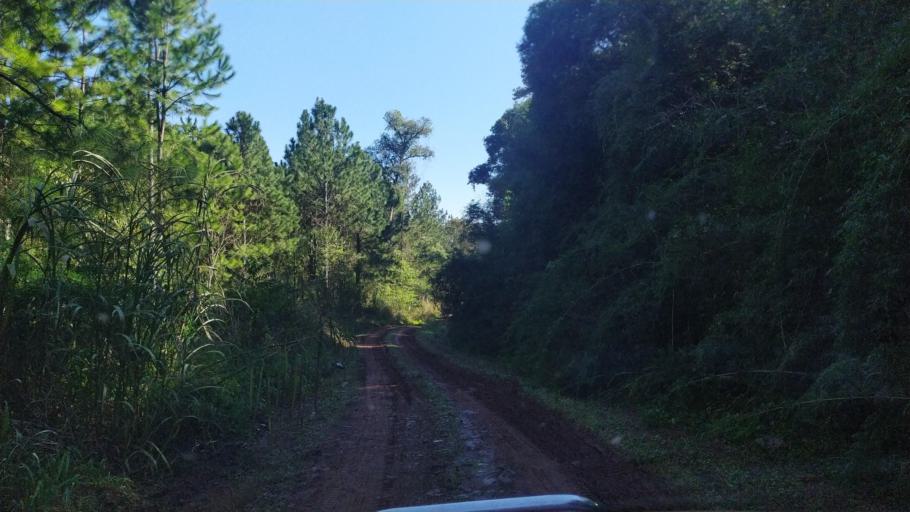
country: AR
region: Misiones
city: El Alcazar
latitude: -26.7551
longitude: -54.5968
